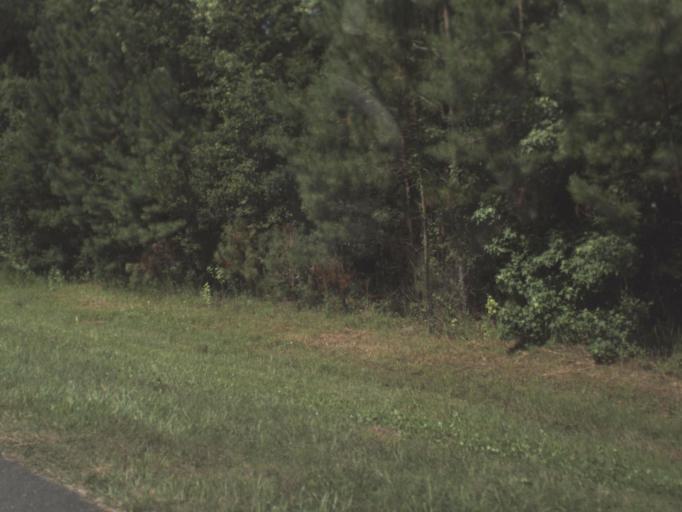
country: US
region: Florida
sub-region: Baker County
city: Macclenny
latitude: 30.2971
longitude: -82.1263
